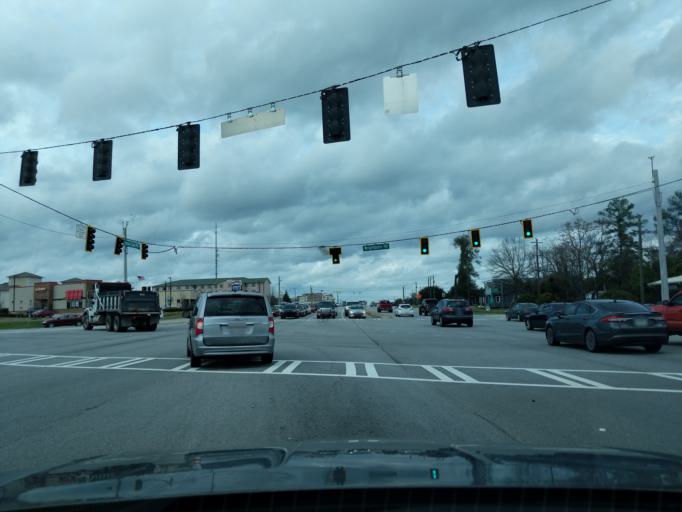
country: US
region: Georgia
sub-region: Columbia County
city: Evans
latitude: 33.4739
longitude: -82.1287
